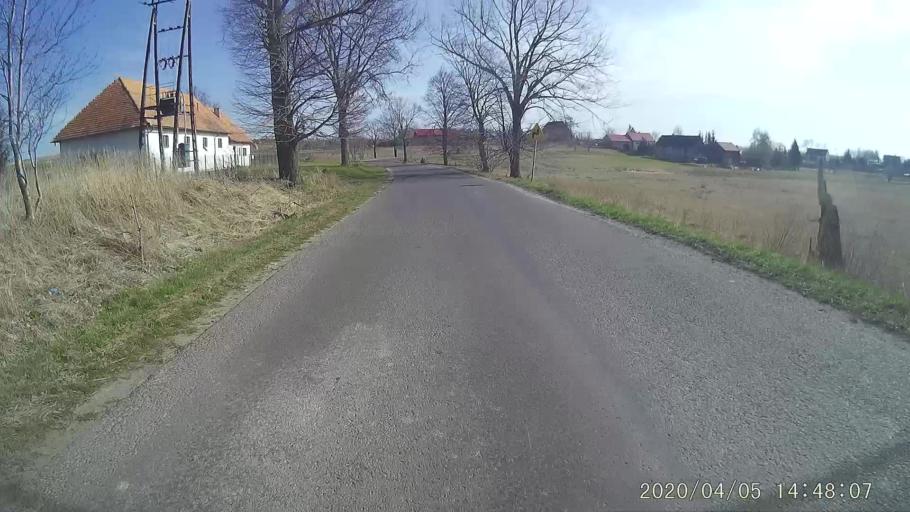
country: PL
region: Lower Silesian Voivodeship
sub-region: Powiat zgorzelecki
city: Sulikow
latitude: 51.0676
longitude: 15.1064
